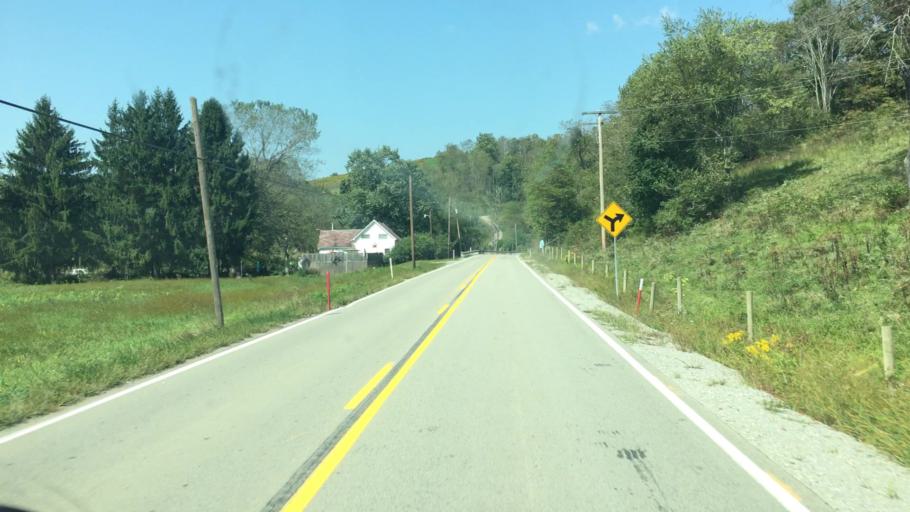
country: US
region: Pennsylvania
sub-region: Greene County
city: Waynesburg
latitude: 39.9535
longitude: -80.3043
